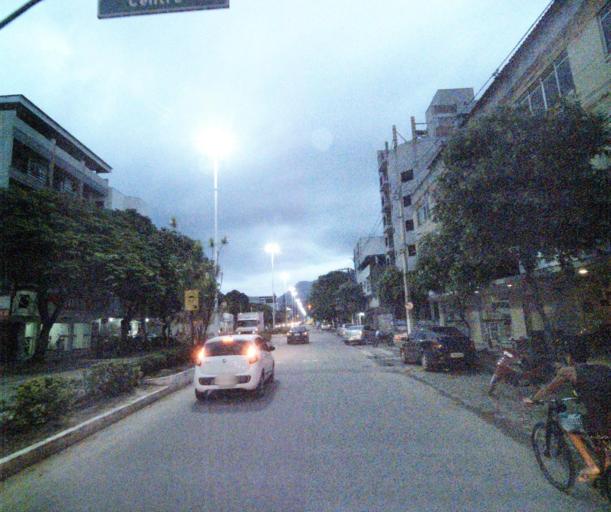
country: BR
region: Espirito Santo
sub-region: Castelo
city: Castelo
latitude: -20.6083
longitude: -41.2039
